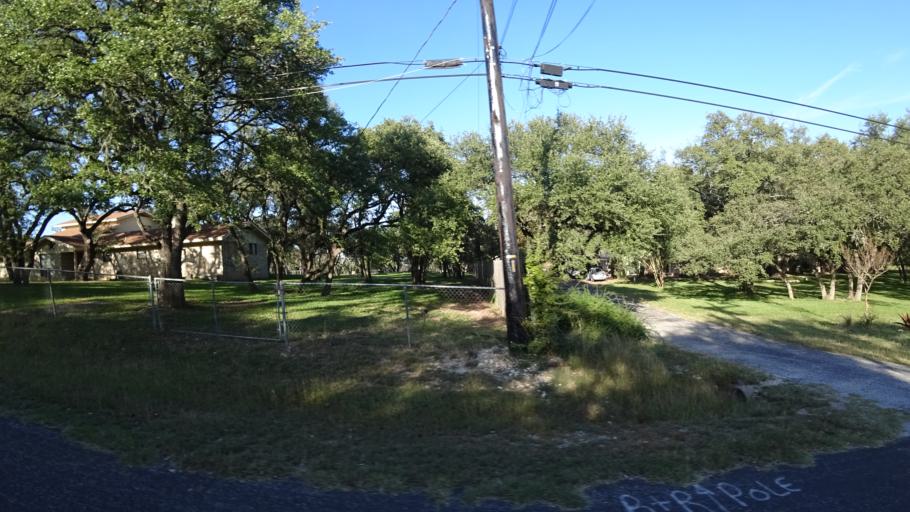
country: US
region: Texas
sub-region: Travis County
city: Barton Creek
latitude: 30.2376
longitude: -97.9118
